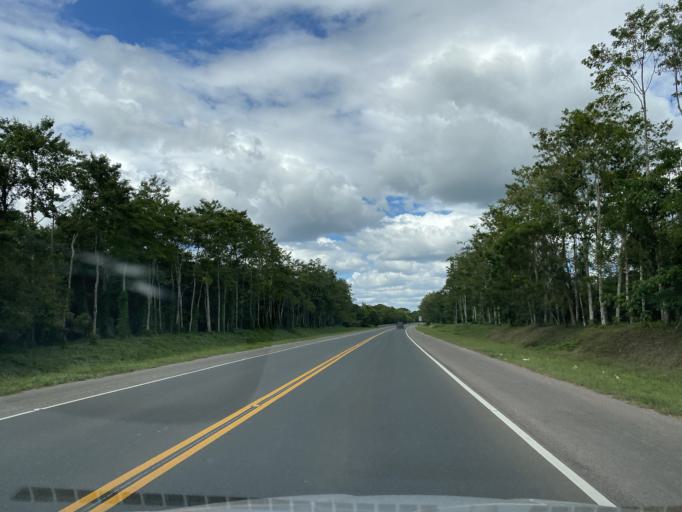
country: DO
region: Santo Domingo
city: Guerra
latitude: 18.5958
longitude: -69.7709
